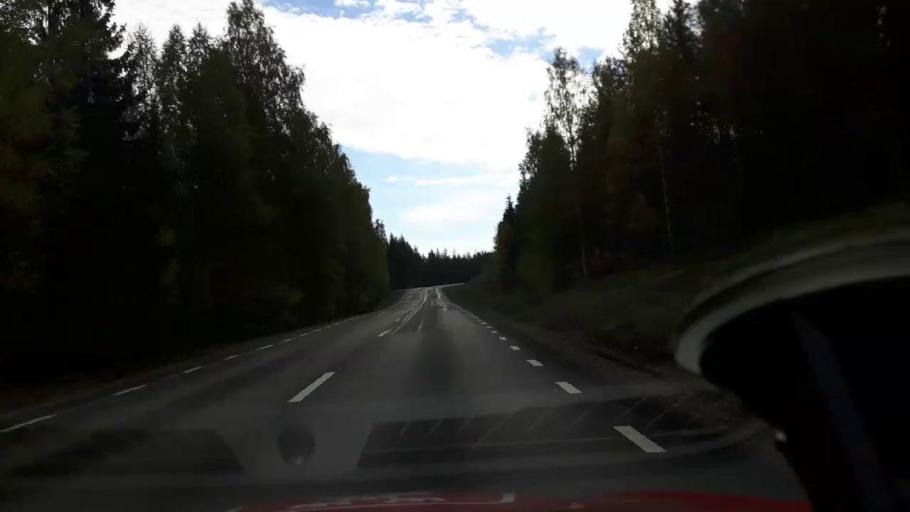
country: SE
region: Gaevleborg
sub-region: Ljusdals Kommun
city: Farila
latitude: 61.9465
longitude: 15.3747
